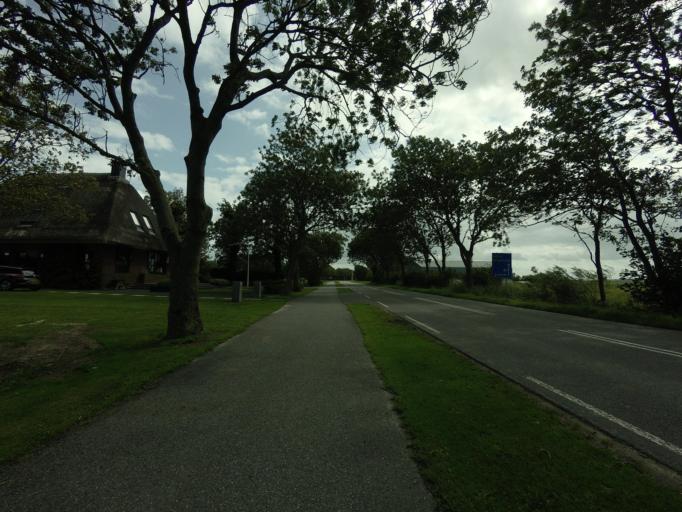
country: NL
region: Friesland
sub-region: Gemeente Harlingen
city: Harlingen
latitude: 53.1346
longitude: 5.4677
